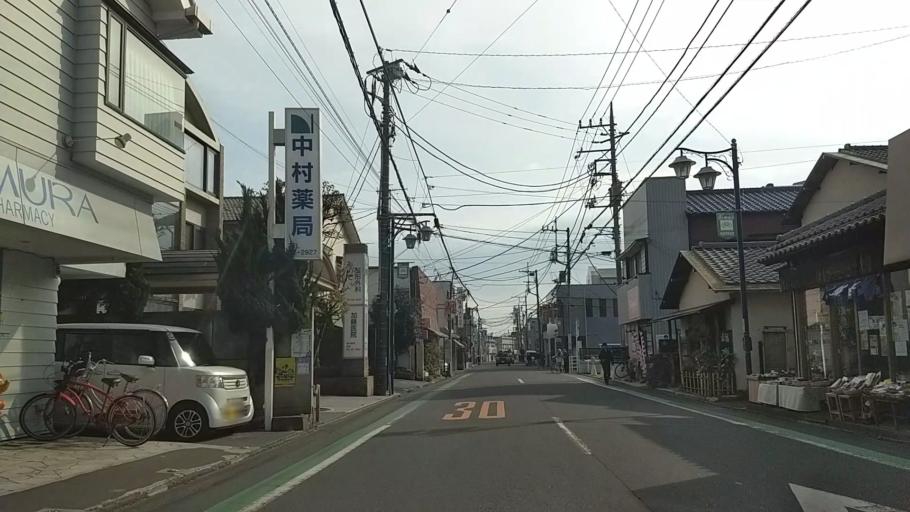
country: JP
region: Kanagawa
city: Chigasaki
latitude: 35.3281
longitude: 139.4077
